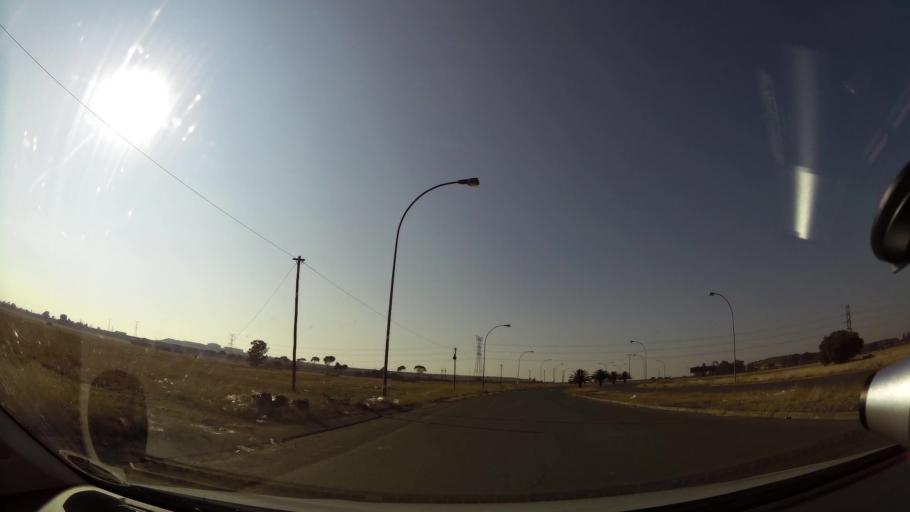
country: ZA
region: Orange Free State
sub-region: Mangaung Metropolitan Municipality
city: Bloemfontein
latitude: -29.1850
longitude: 26.1842
